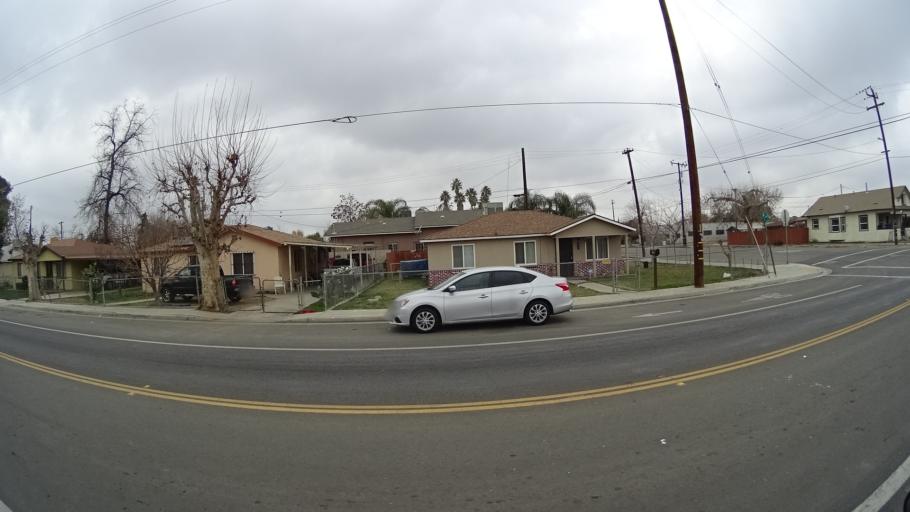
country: US
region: California
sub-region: Kern County
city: Bakersfield
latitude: 35.3643
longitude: -119.0118
